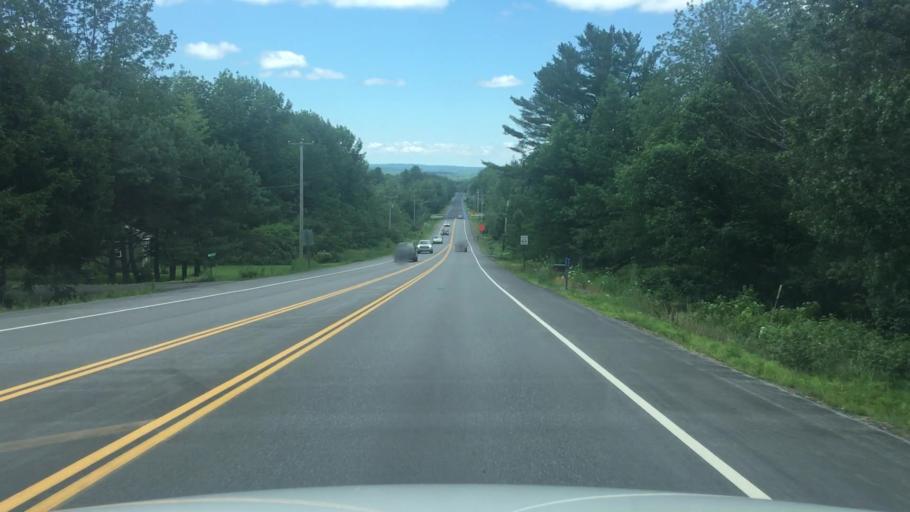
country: US
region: Maine
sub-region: Waldo County
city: Searsmont
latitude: 44.3976
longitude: -69.1396
